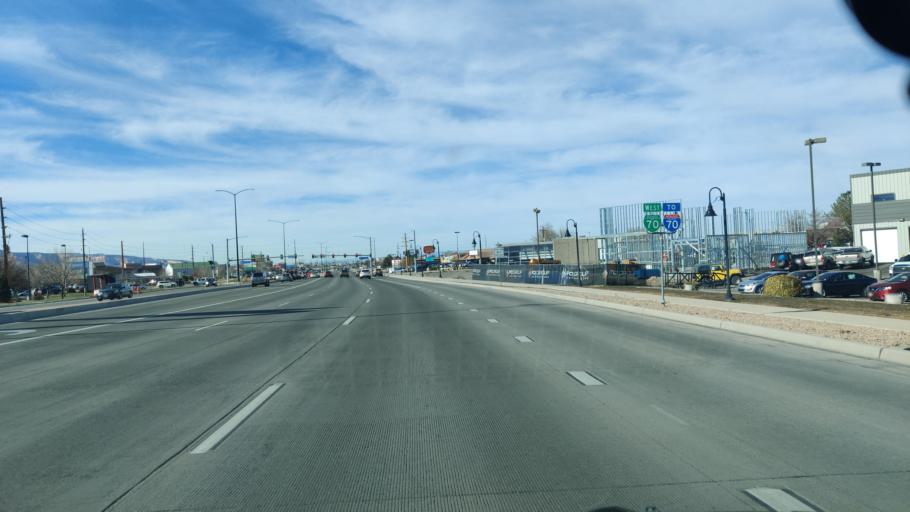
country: US
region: Colorado
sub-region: Mesa County
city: Grand Junction
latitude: 39.0798
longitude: -108.5813
